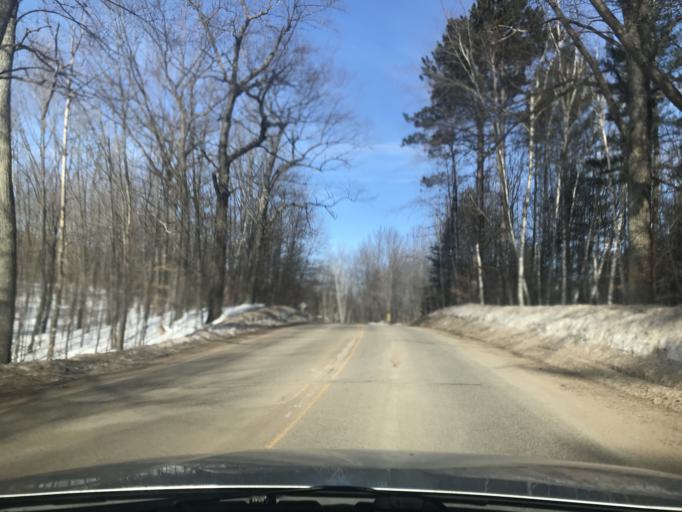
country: US
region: Michigan
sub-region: Dickinson County
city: Kingsford
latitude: 45.4011
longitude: -88.3416
